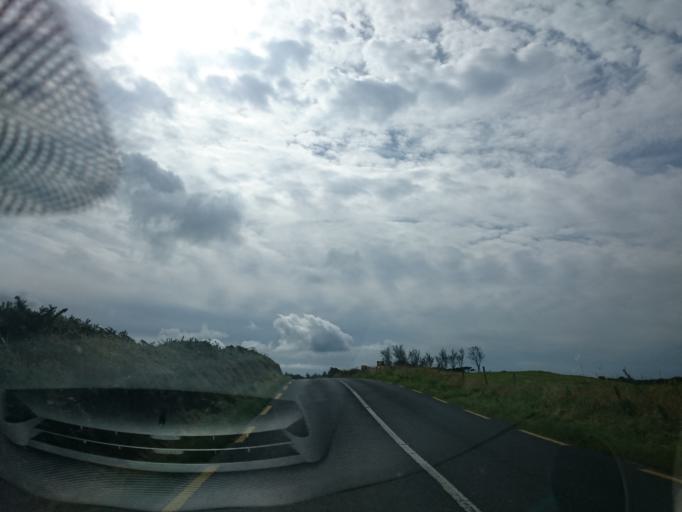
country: IE
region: Munster
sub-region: Waterford
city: Tra Mhor
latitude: 52.1782
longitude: -7.1678
